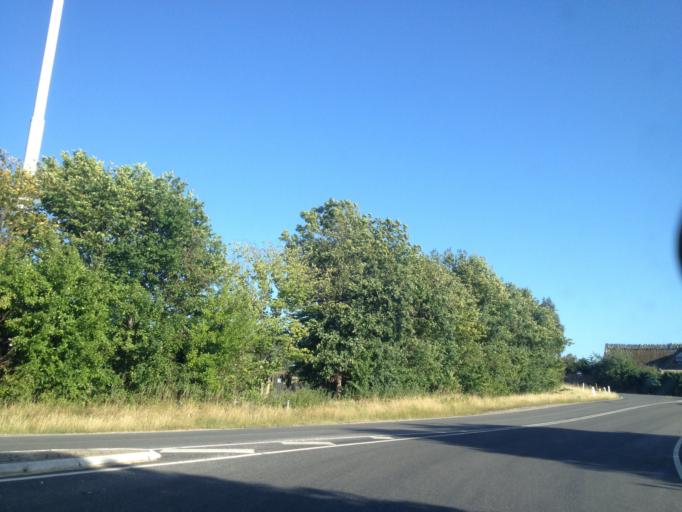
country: DK
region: Capital Region
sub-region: Gribskov Kommune
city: Helsinge
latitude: 56.0161
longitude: 12.1462
